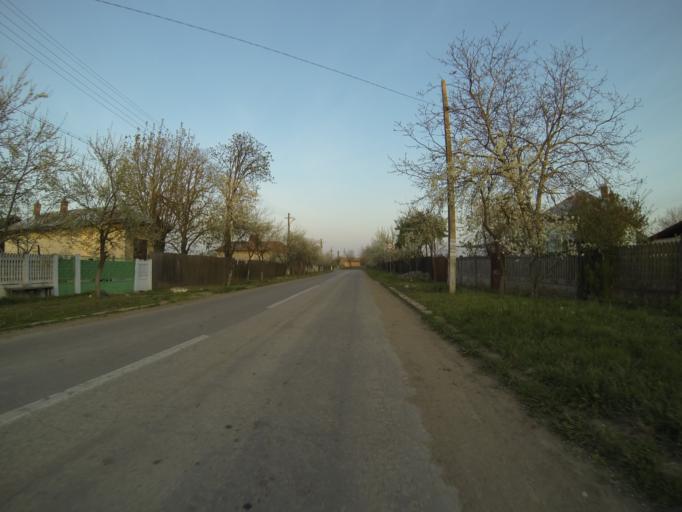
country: RO
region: Dolj
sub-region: Comuna Dranicu
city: Dranic
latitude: 44.0565
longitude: 23.8364
